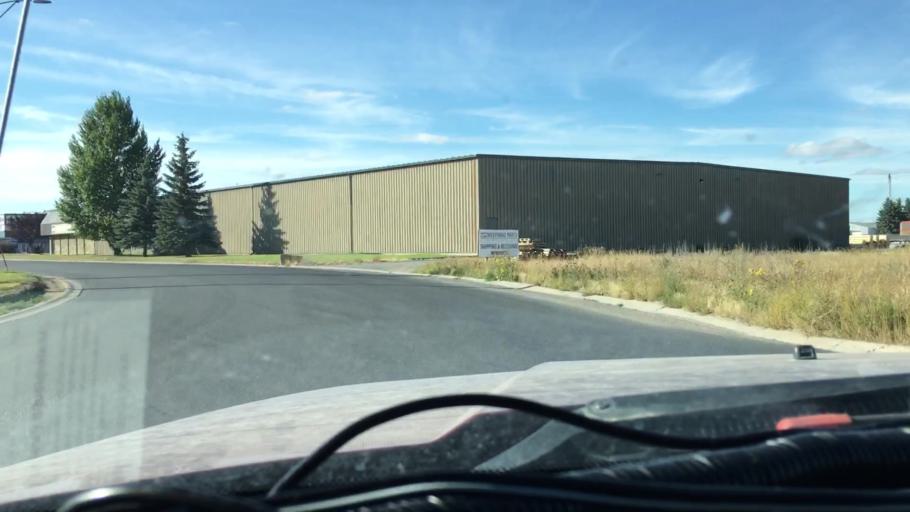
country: CA
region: Saskatchewan
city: Regina
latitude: 50.4780
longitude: -104.5617
